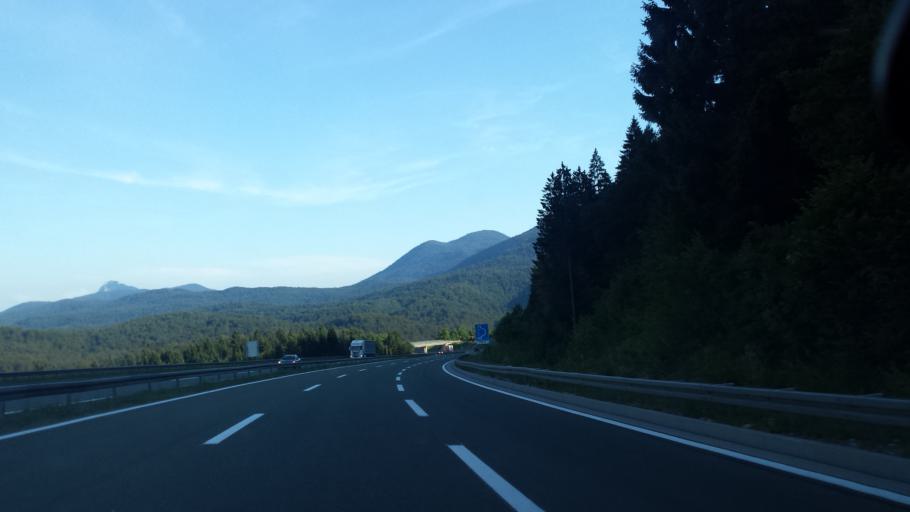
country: HR
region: Primorsko-Goranska
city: Vrbovsko
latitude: 45.3675
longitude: 15.0596
